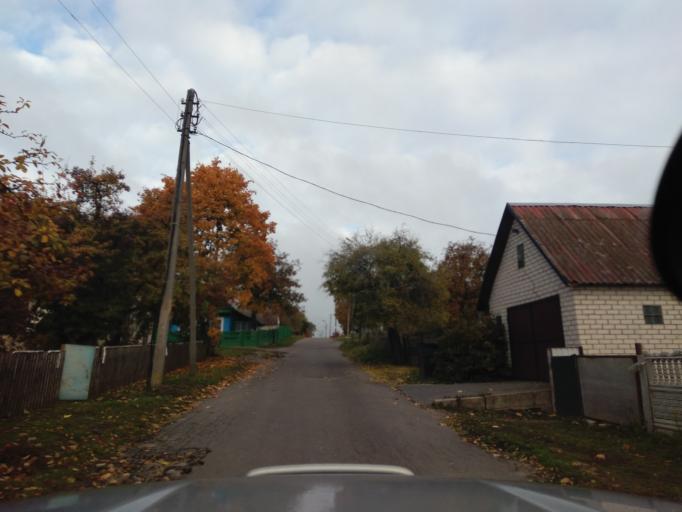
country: BY
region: Minsk
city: Kapyl'
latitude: 53.1577
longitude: 27.0848
